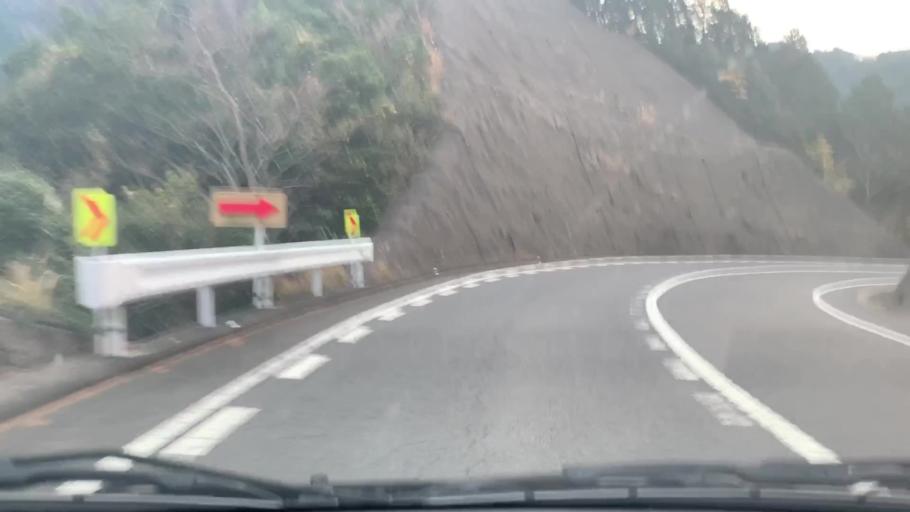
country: JP
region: Nagasaki
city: Omura
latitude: 32.9820
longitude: 130.0389
